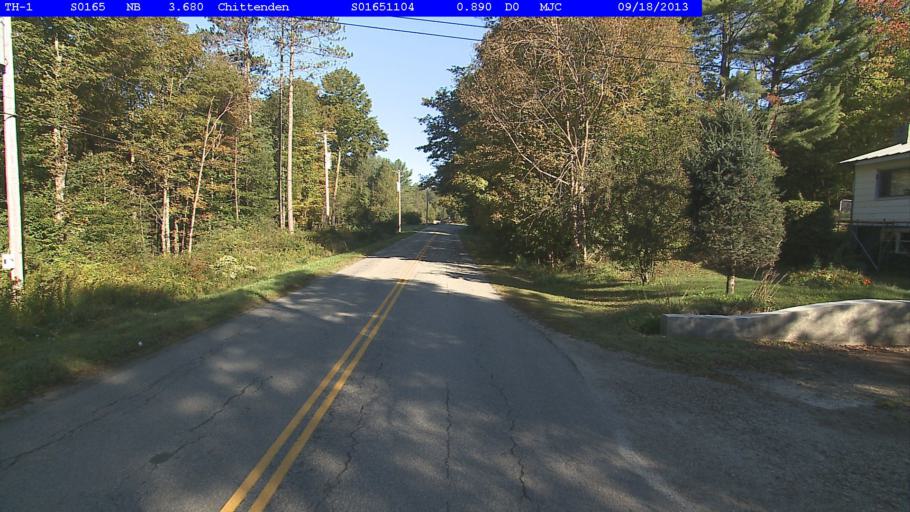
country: US
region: Vermont
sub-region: Rutland County
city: Rutland
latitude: 43.6896
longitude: -72.9526
